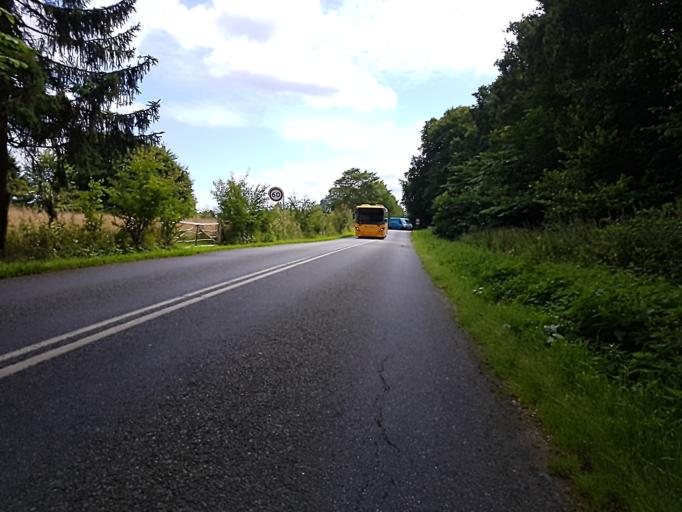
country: DK
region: Capital Region
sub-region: Fureso Kommune
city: Farum
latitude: 55.8090
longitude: 12.3248
